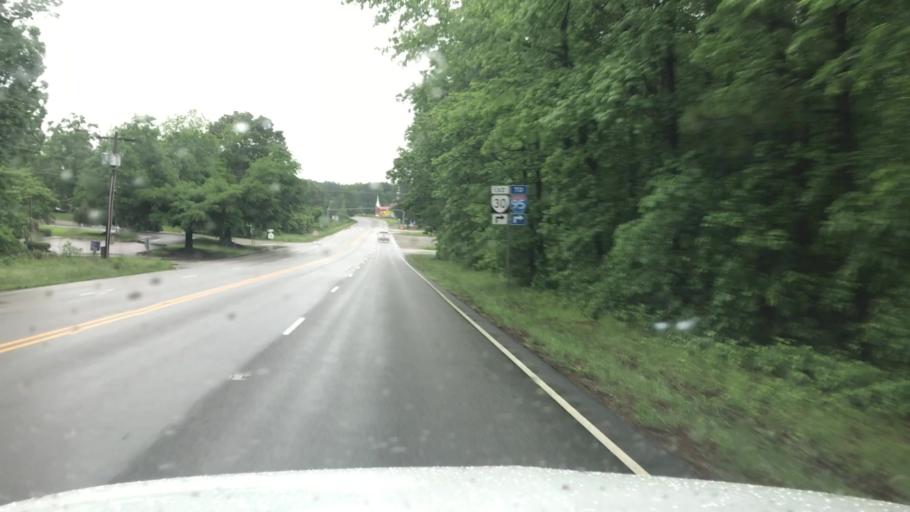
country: US
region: Virginia
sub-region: Hanover County
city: Ashland
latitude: 37.8435
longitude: -77.4655
